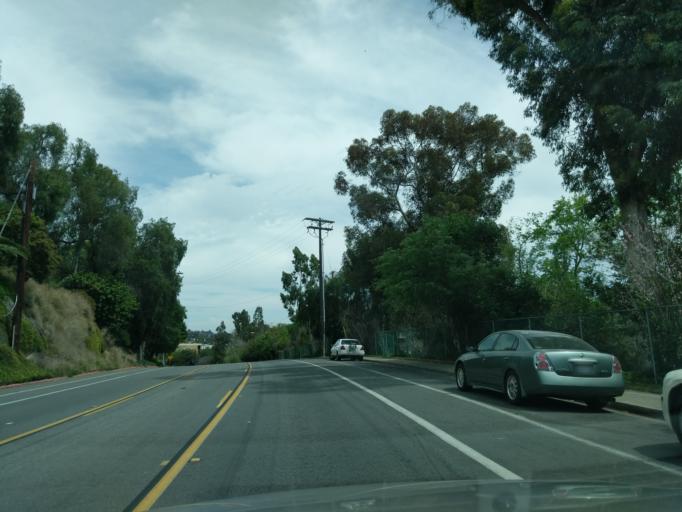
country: US
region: California
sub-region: San Diego County
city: La Mesa
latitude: 32.7838
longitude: -117.1062
